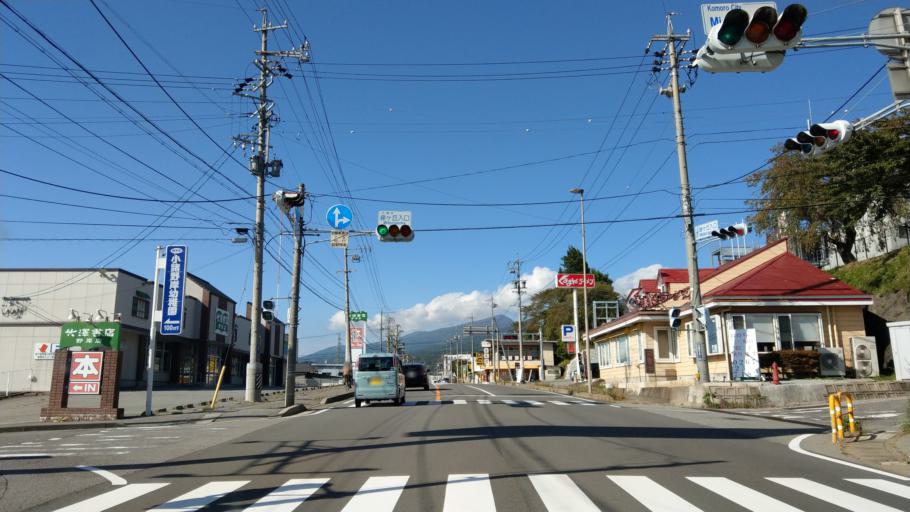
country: JP
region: Nagano
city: Komoro
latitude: 36.3251
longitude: 138.4357
